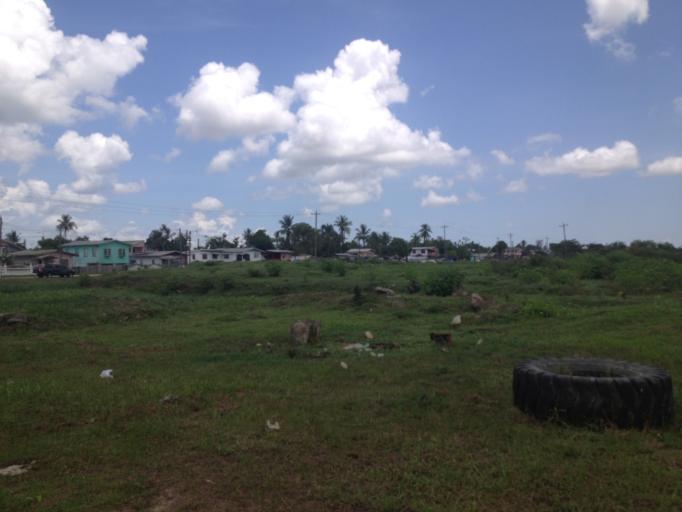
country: GY
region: Demerara-Mahaica
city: Georgetown
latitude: 6.7036
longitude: -58.1851
